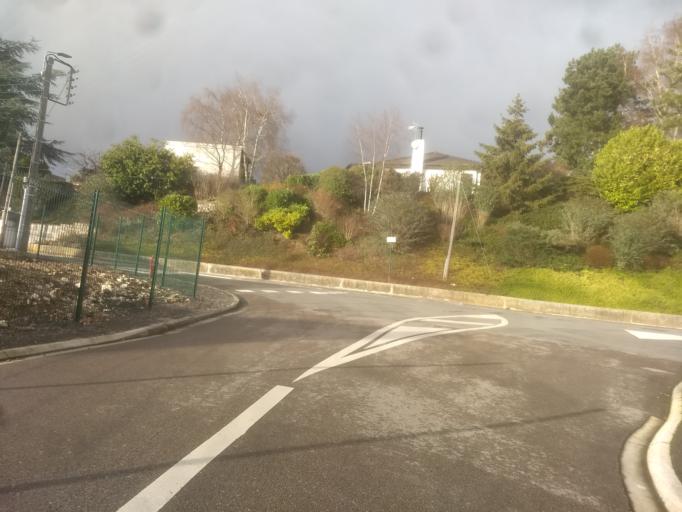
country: FR
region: Nord-Pas-de-Calais
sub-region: Departement du Pas-de-Calais
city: Saint-Laurent-Blangy
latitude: 50.3036
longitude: 2.8071
